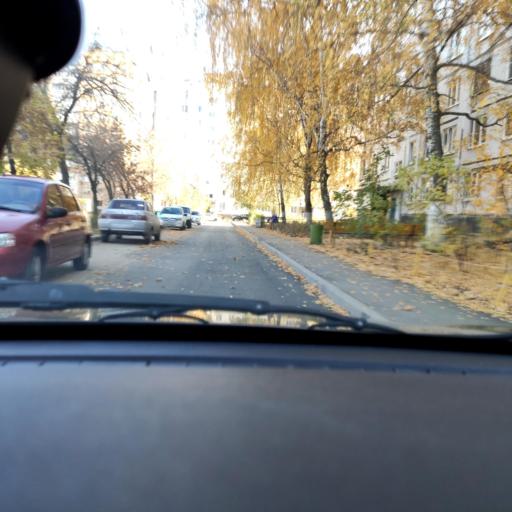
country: RU
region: Samara
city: Tol'yatti
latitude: 53.5324
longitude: 49.2741
